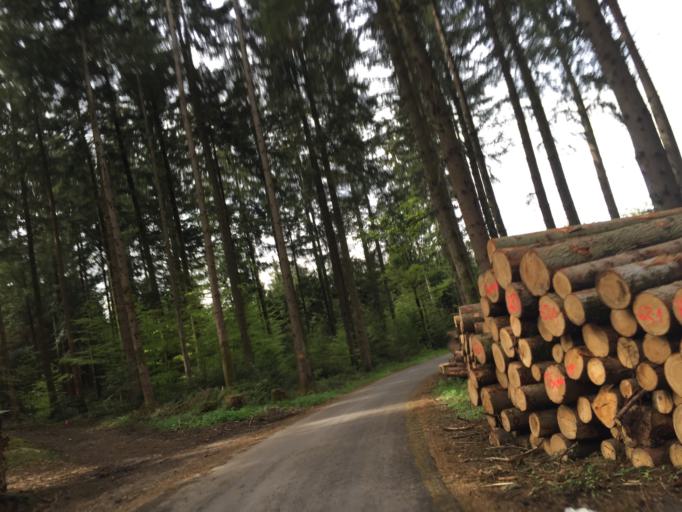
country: CH
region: Bern
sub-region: Bern-Mittelland District
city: Muri
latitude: 46.9240
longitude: 7.5195
